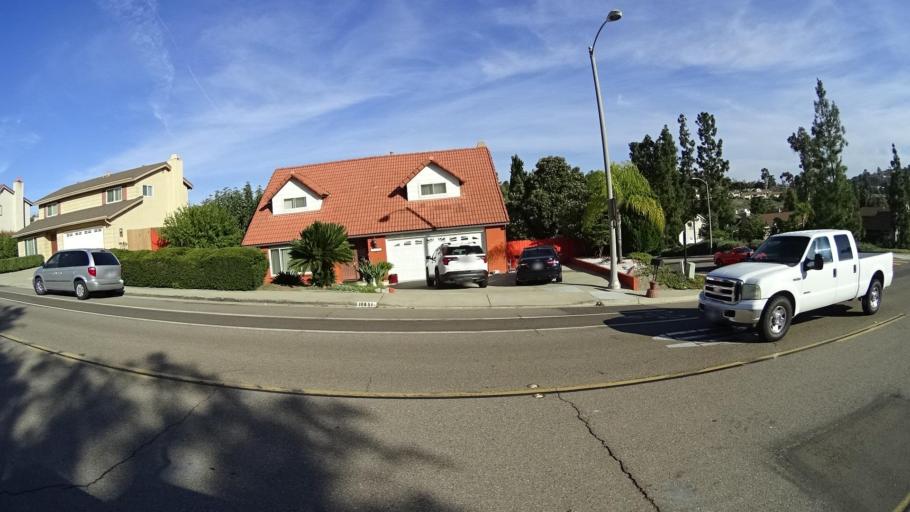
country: US
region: California
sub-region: San Diego County
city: Spring Valley
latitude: 32.7315
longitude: -116.9785
